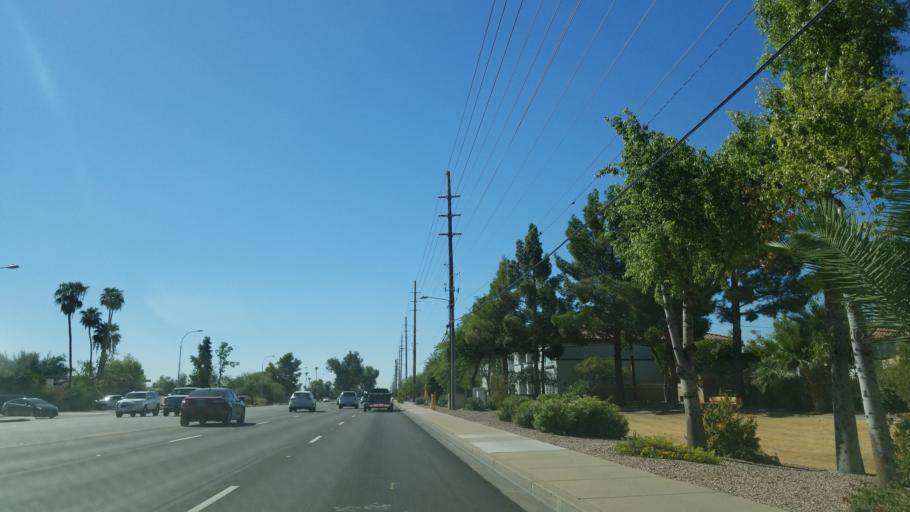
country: US
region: Arizona
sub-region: Maricopa County
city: Scottsdale
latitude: 33.4767
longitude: -111.9090
